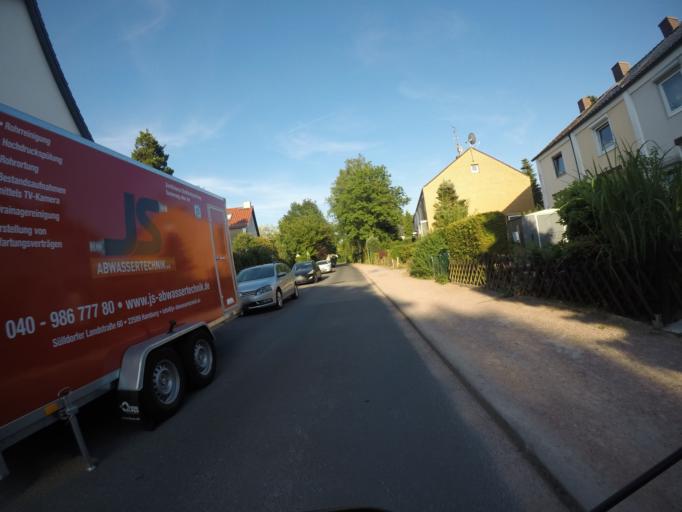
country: DE
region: Schleswig-Holstein
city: Rellingen
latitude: 53.5797
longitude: 9.7894
